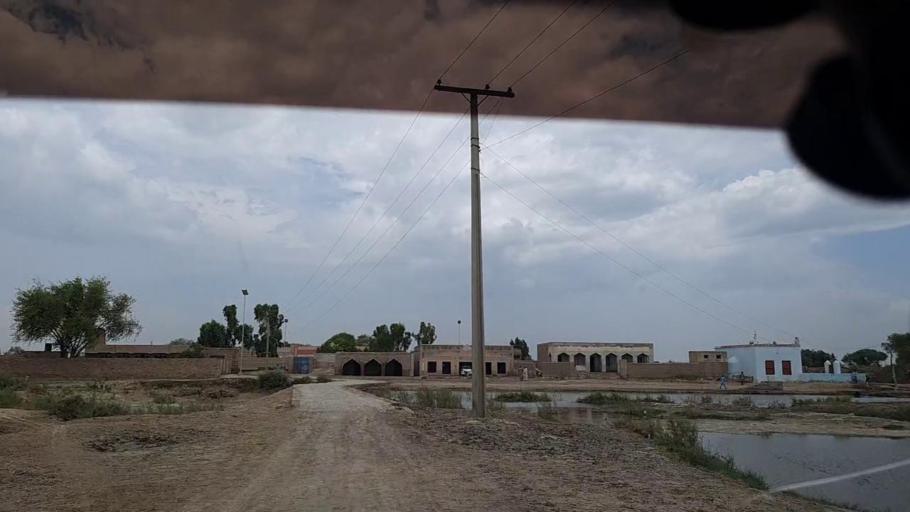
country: PK
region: Sindh
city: Ghauspur
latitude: 28.1155
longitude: 68.9884
